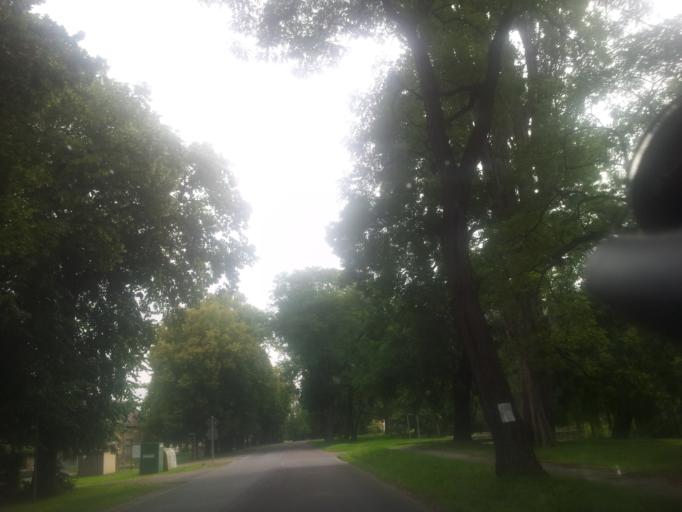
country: DE
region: Saxony-Anhalt
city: Giersleben
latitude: 51.7797
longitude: 11.5806
